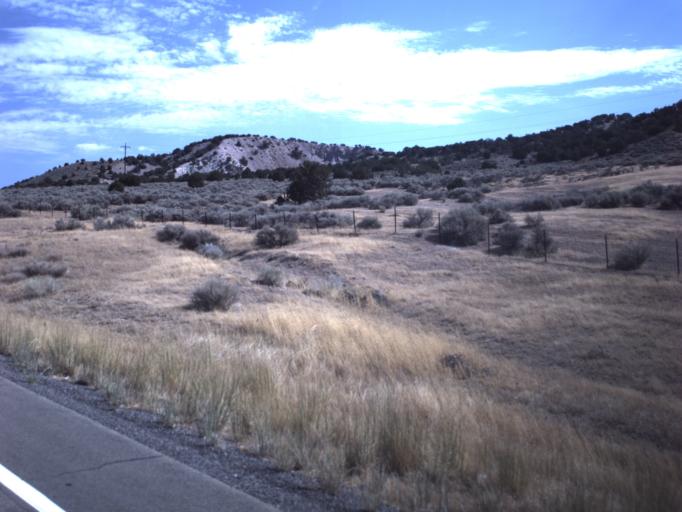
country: US
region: Utah
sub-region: Sanpete County
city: Gunnison
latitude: 39.4129
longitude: -111.9247
